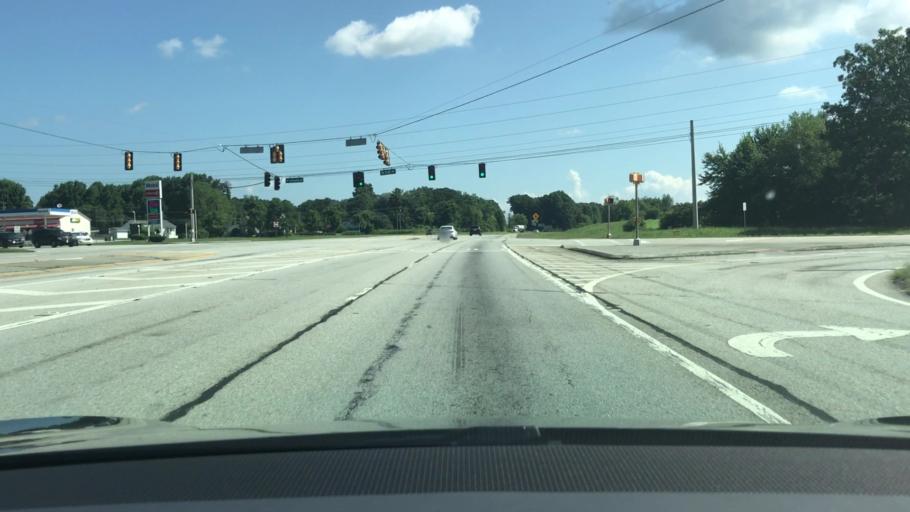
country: US
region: Georgia
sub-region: Habersham County
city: Clarkesville
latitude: 34.6458
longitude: -83.4496
